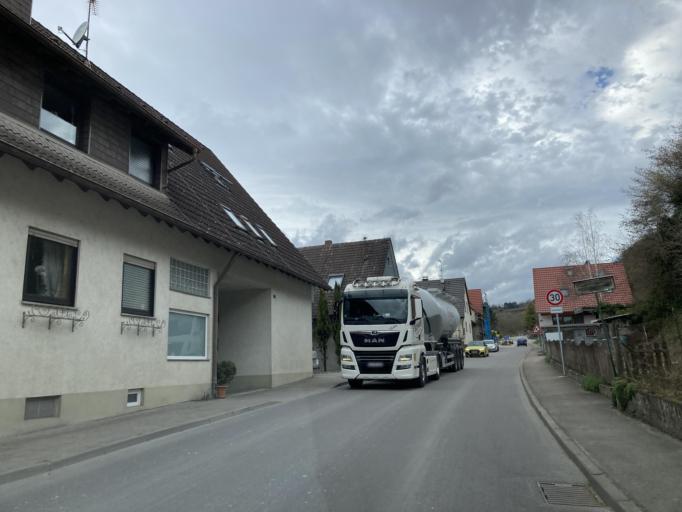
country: DE
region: Baden-Wuerttemberg
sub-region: Freiburg Region
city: Botzingen
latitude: 48.0746
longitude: 7.7061
